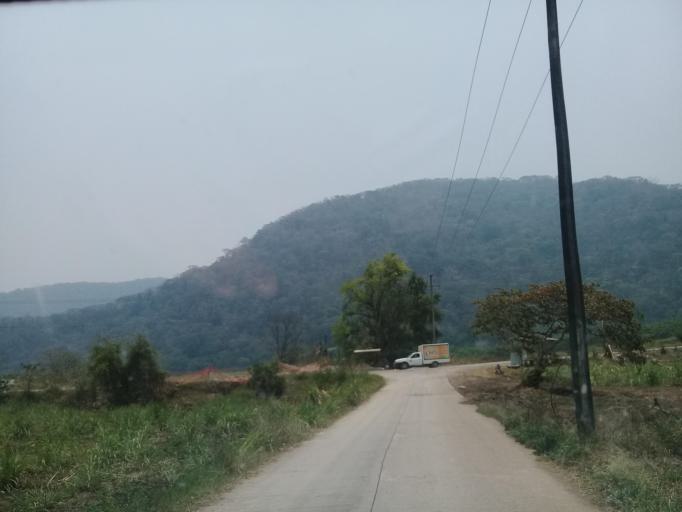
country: MX
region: Veracruz
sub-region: Tezonapa
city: Laguna Chica (Pueblo Nuevo)
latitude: 18.5683
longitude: -96.7208
